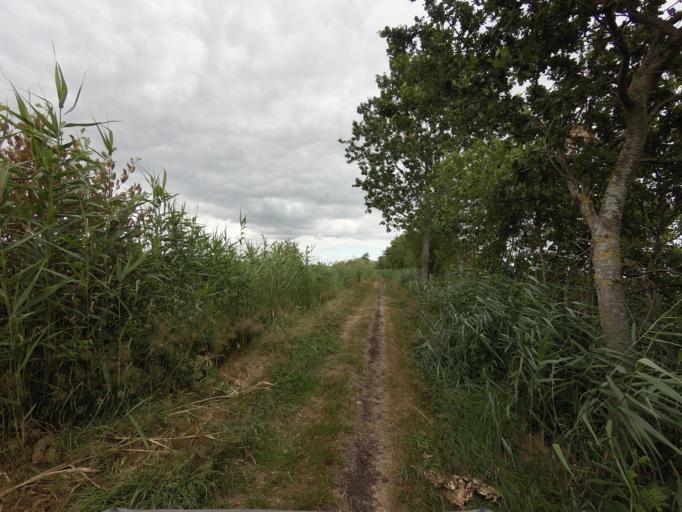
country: NL
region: Utrecht
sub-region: Stichtse Vecht
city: Breukelen
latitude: 52.1846
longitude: 4.9442
